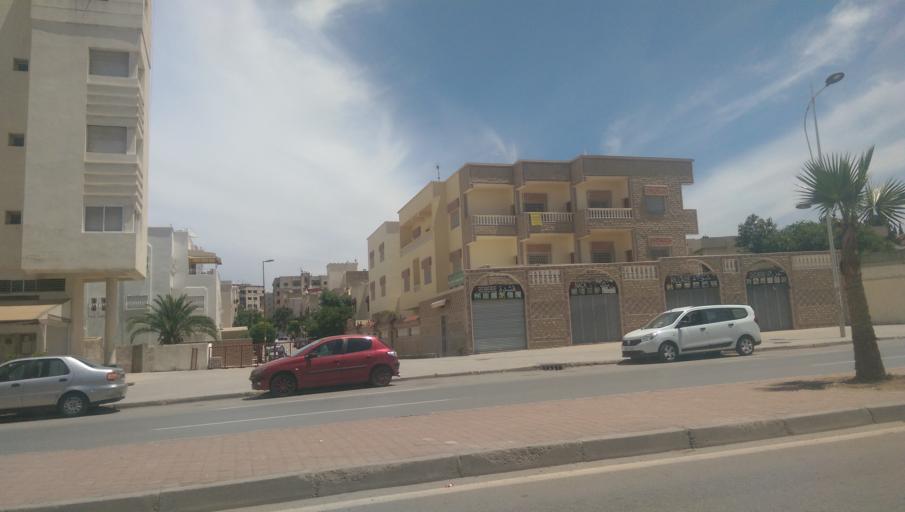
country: MA
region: Fes-Boulemane
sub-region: Fes
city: Fes
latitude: 34.0169
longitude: -4.9848
